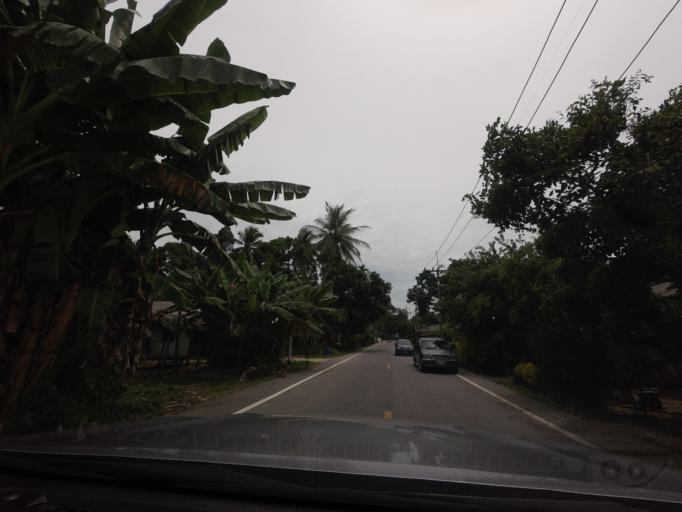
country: TH
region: Pattani
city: Kapho
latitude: 6.6416
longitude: 101.5502
